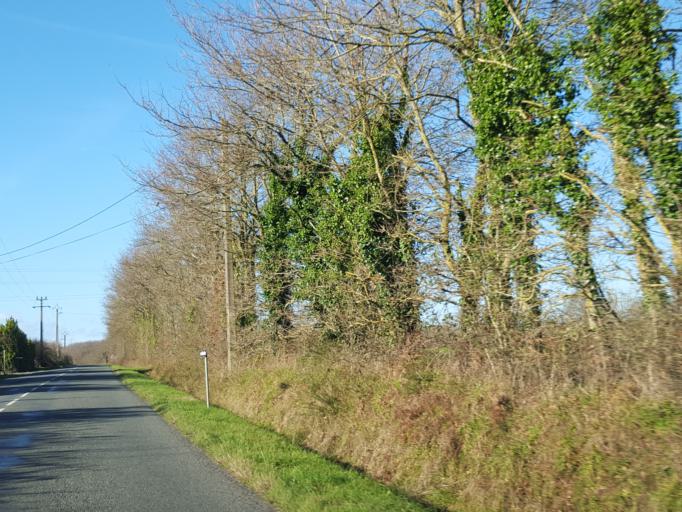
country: FR
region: Pays de la Loire
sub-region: Departement de la Vendee
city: La Roche-sur-Yon
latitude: 46.6705
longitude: -1.4739
